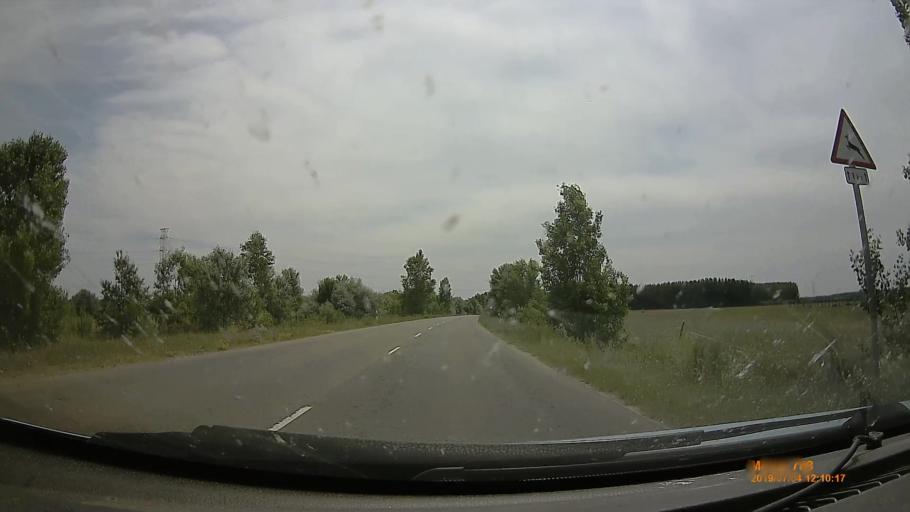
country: HU
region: Pest
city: Gyal
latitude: 47.3849
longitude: 19.2499
